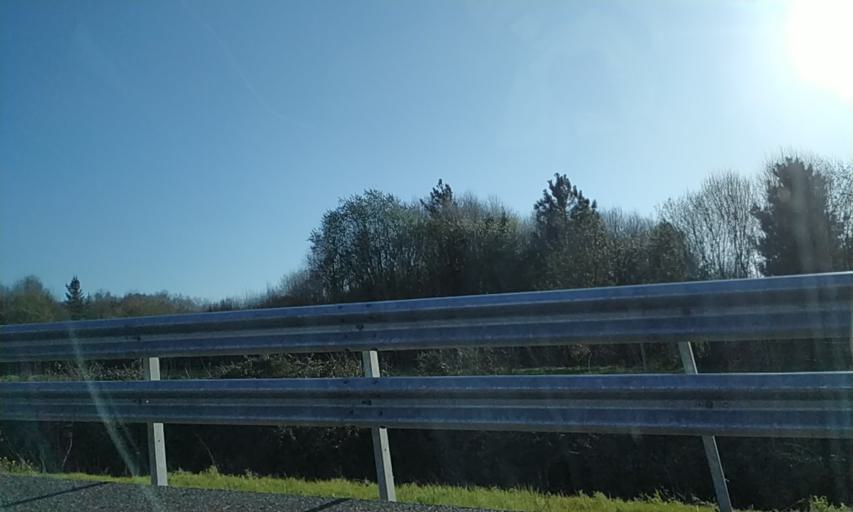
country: ES
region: Galicia
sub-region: Provincia de Lugo
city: Outeiro de Rei
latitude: 43.0659
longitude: -7.5712
